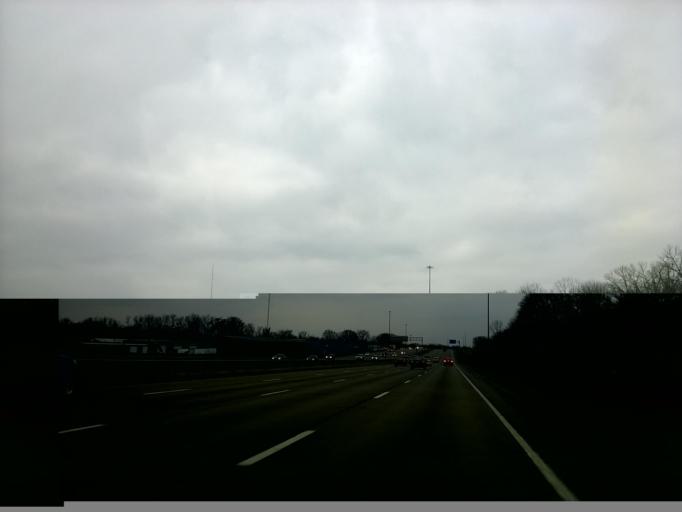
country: US
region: Indiana
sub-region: Marion County
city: Warren Park
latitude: 39.8055
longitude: -86.0673
